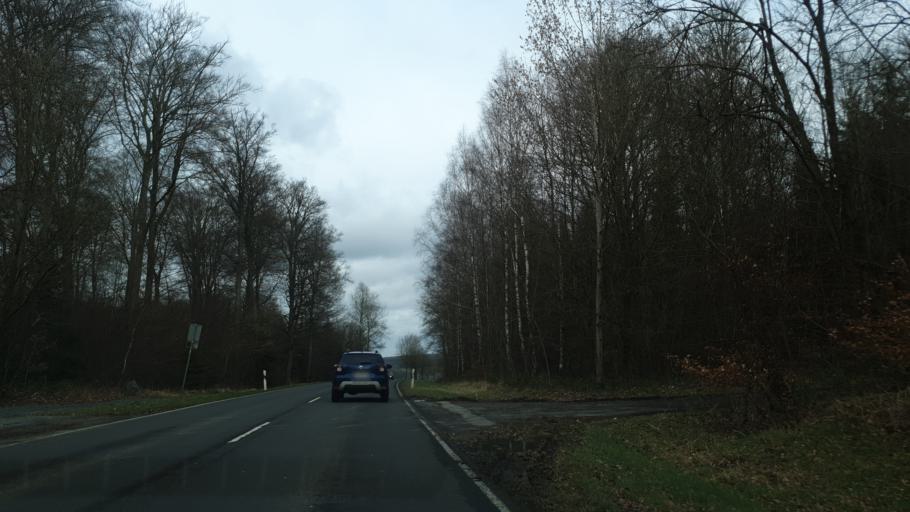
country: DE
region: Rheinland-Pfalz
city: Harschbach
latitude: 50.5856
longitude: 7.5993
